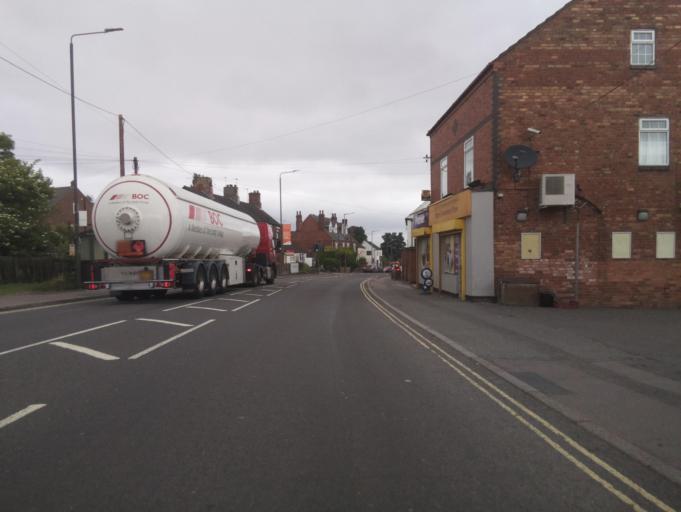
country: GB
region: England
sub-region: Derbyshire
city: Swadlincote
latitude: 52.7654
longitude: -1.5281
